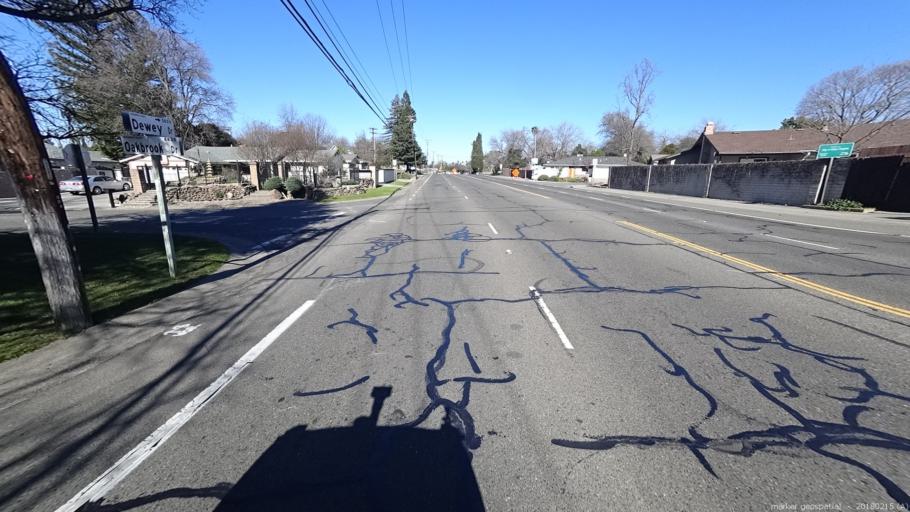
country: US
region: California
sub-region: Sacramento County
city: Antelope
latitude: 38.6713
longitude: -121.3089
